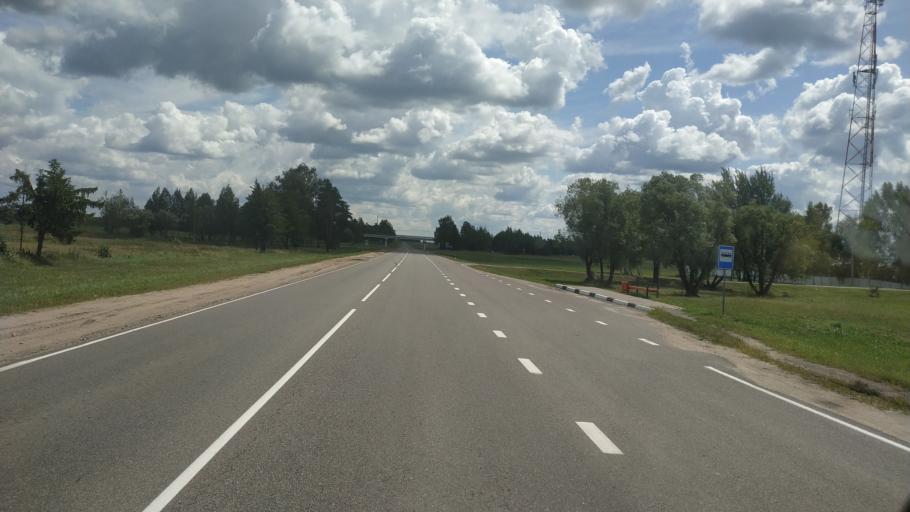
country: BY
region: Mogilev
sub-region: Mahilyowski Rayon
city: Veyno
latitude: 53.8144
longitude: 30.4523
